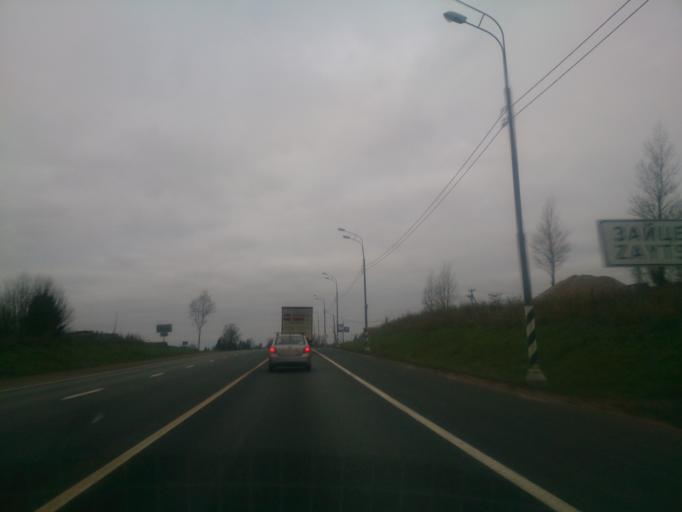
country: RU
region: Novgorod
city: Proletariy
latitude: 58.3673
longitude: 32.0869
